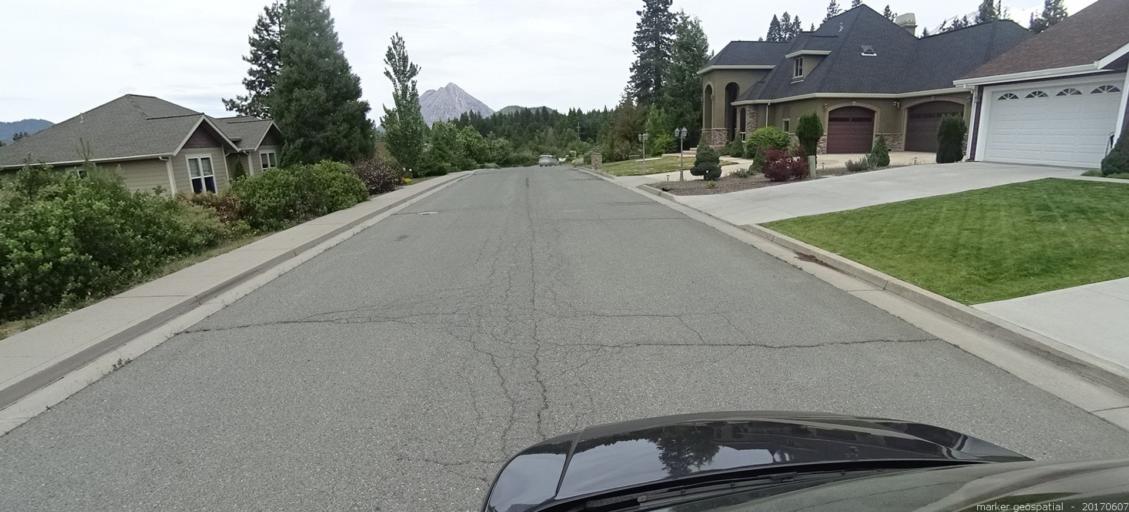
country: US
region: California
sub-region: Siskiyou County
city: Mount Shasta
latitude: 41.2928
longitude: -122.3131
